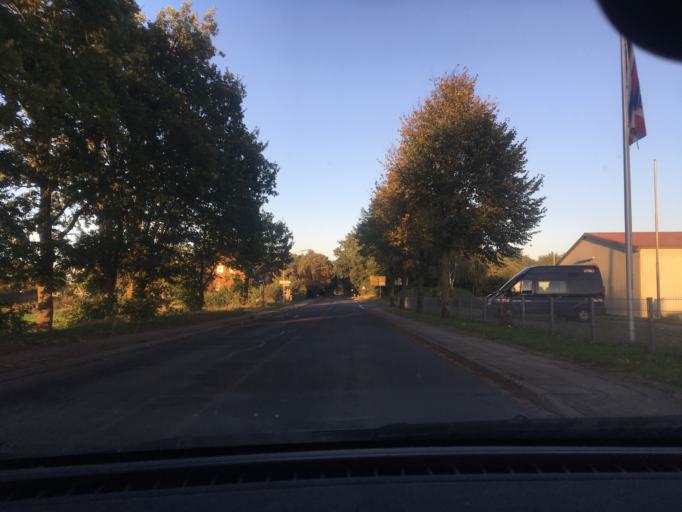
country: DE
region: Lower Saxony
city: Deutsch Evern
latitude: 53.2049
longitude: 10.4454
